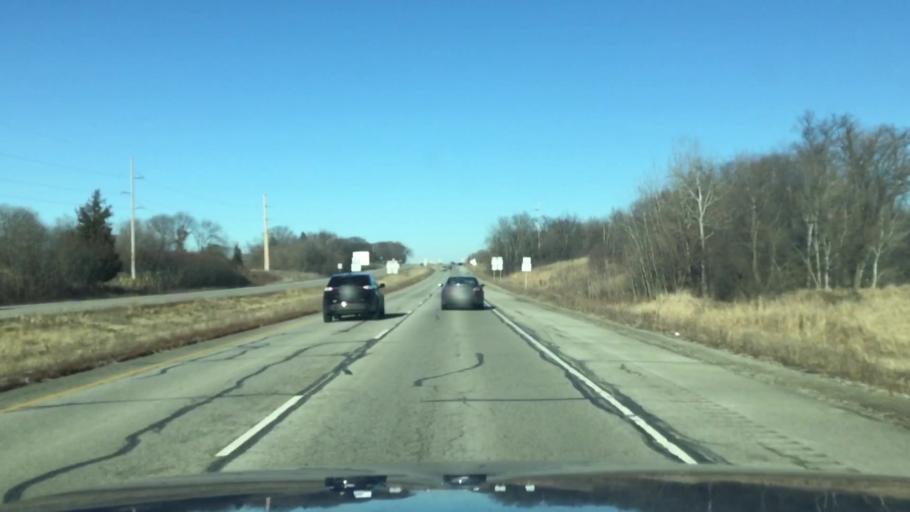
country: US
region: Wisconsin
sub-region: Racine County
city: Rochester
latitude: 42.7318
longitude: -88.2195
